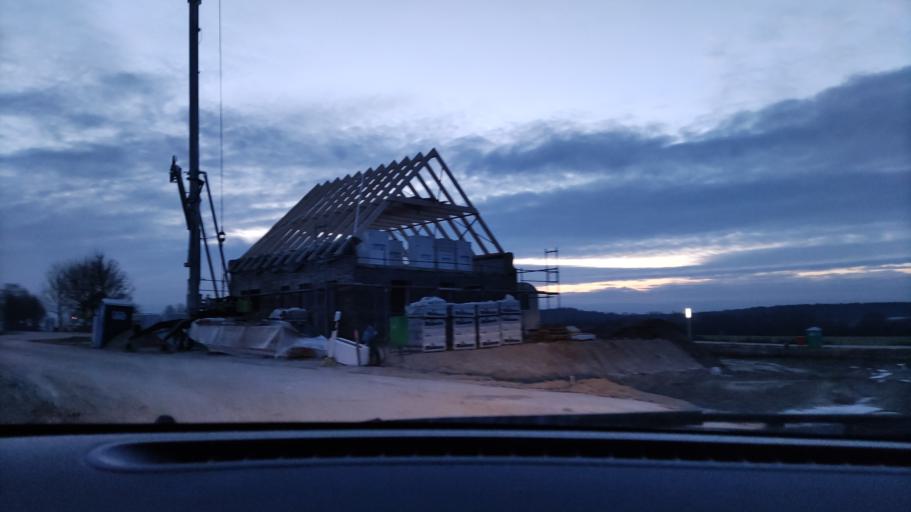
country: DE
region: Mecklenburg-Vorpommern
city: Boizenburg
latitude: 53.3778
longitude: 10.7037
